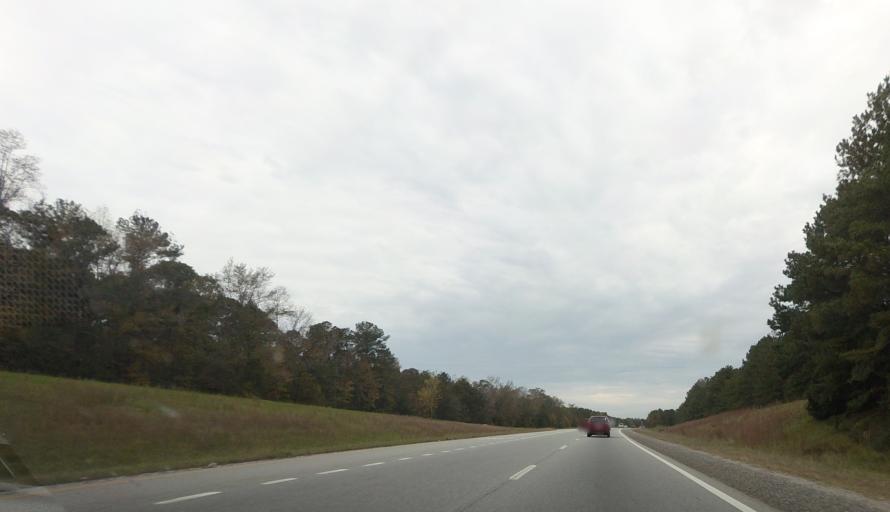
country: US
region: Alabama
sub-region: Lee County
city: Opelika
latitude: 32.6363
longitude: -85.3013
